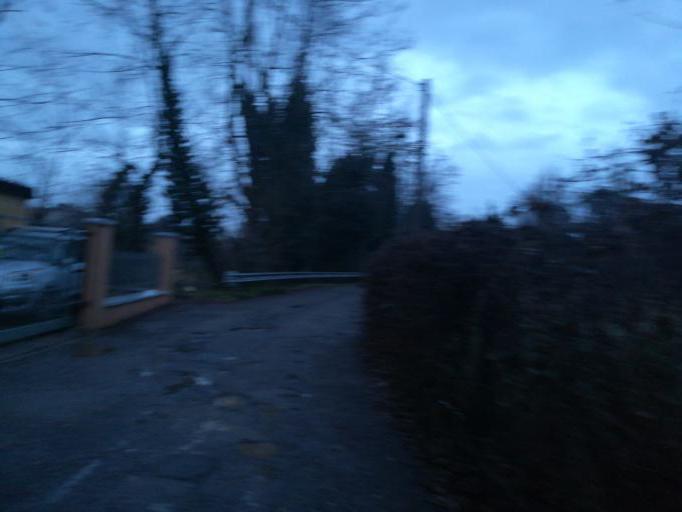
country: IT
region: Emilia-Romagna
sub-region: Provincia di Bologna
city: Progresso
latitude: 44.5468
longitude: 11.3521
